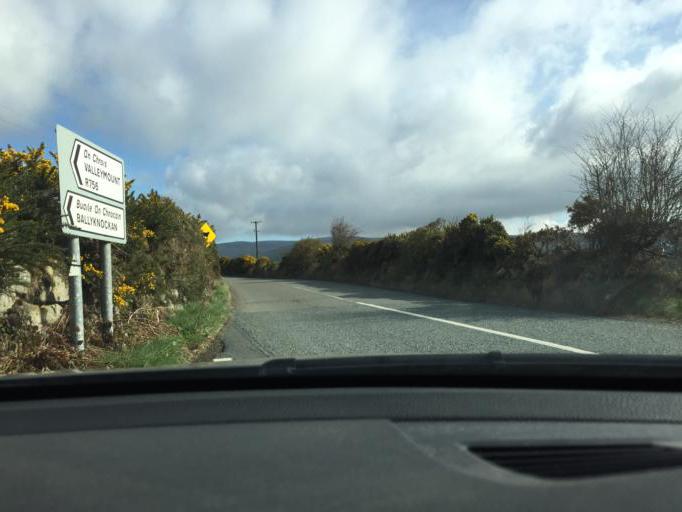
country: IE
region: Leinster
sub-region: Wicklow
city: Valleymount
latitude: 53.0687
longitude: -6.5317
